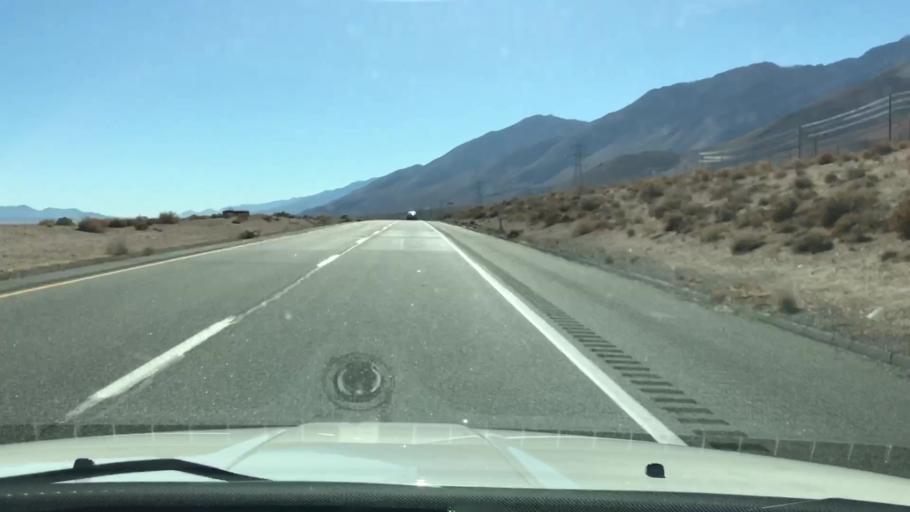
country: US
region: California
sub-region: Inyo County
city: Lone Pine
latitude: 36.4797
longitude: -118.0356
